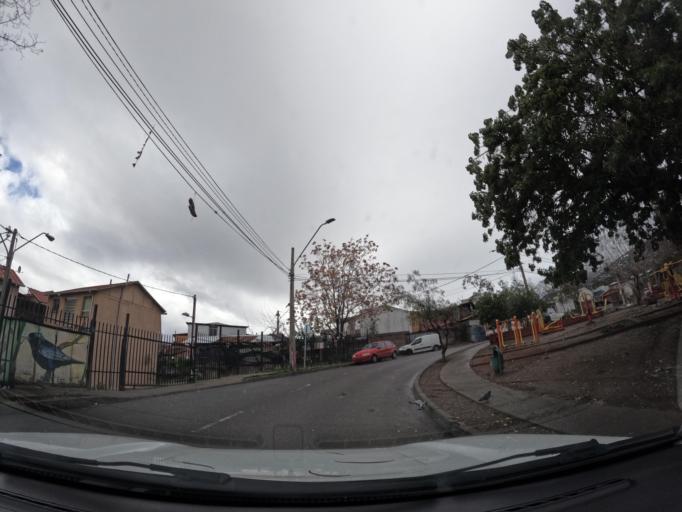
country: CL
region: Santiago Metropolitan
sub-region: Provincia de Santiago
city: Villa Presidente Frei, Nunoa, Santiago, Chile
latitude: -33.4825
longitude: -70.5250
